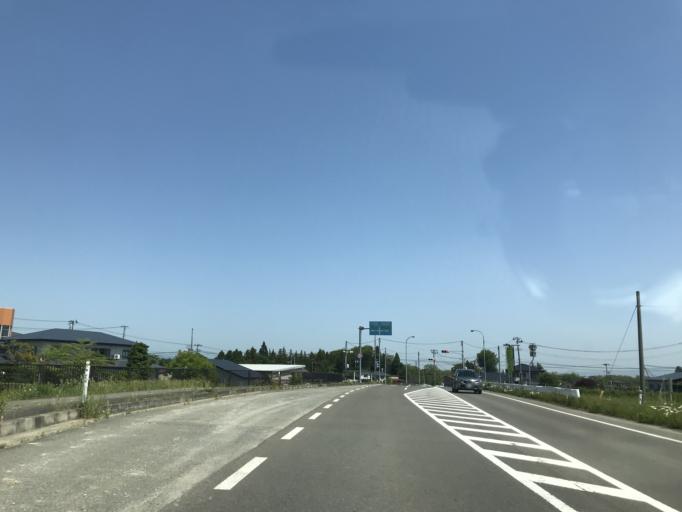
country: JP
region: Iwate
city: Kitakami
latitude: 39.2819
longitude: 141.0510
